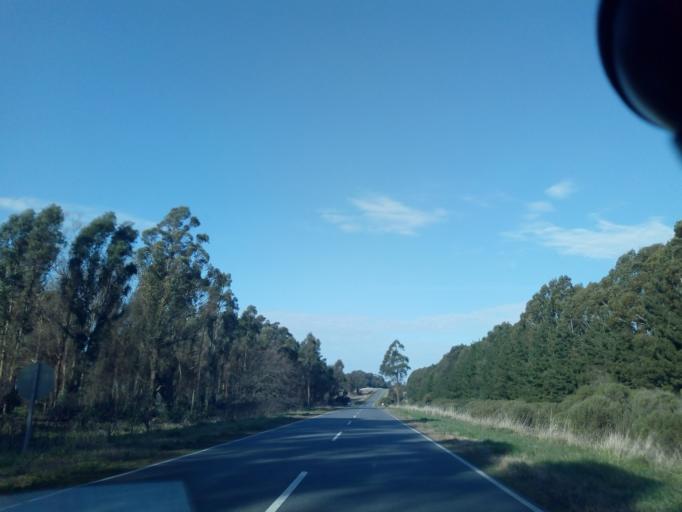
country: AR
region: Buenos Aires
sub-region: Partido de Tandil
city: Tandil
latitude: -37.3500
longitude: -58.8920
